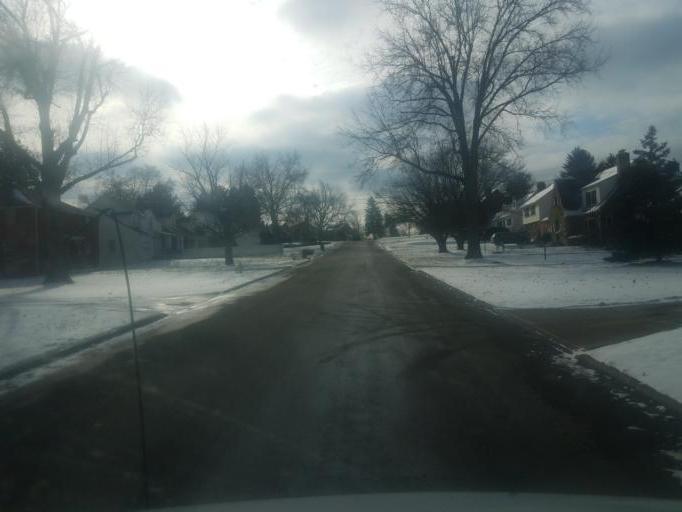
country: US
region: Ohio
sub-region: Richland County
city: Mansfield
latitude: 40.7354
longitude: -82.5340
